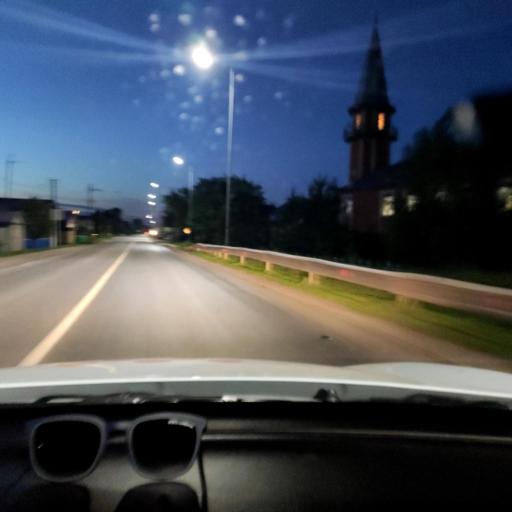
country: RU
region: Tatarstan
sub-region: Alekseyevskiy Rayon
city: Alekseyevskoye
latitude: 55.4257
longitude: 49.8850
